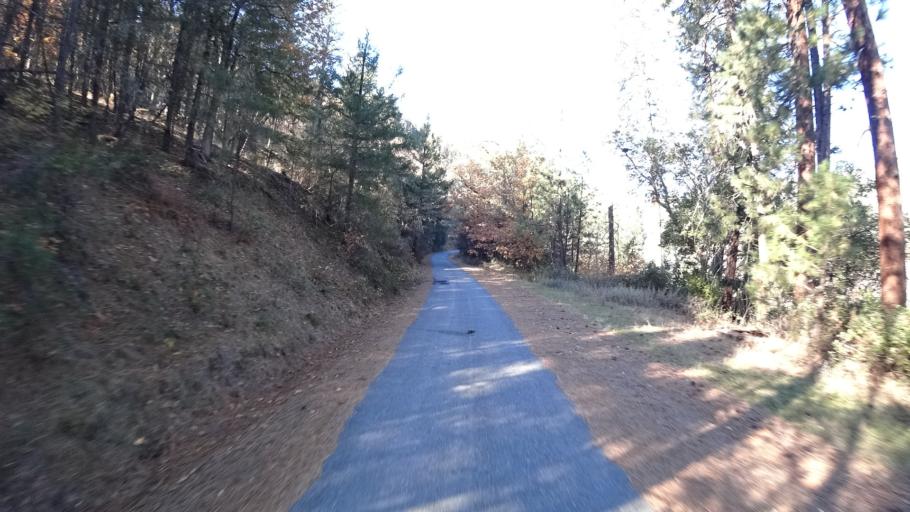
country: US
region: California
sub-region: Siskiyou County
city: Yreka
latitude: 41.8424
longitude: -122.8968
